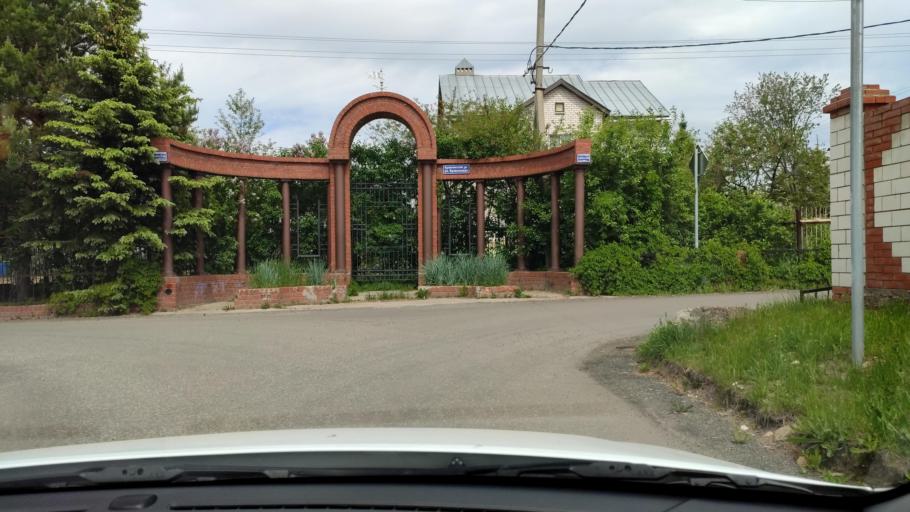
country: RU
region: Tatarstan
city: Vysokaya Gora
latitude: 55.8252
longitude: 49.2324
